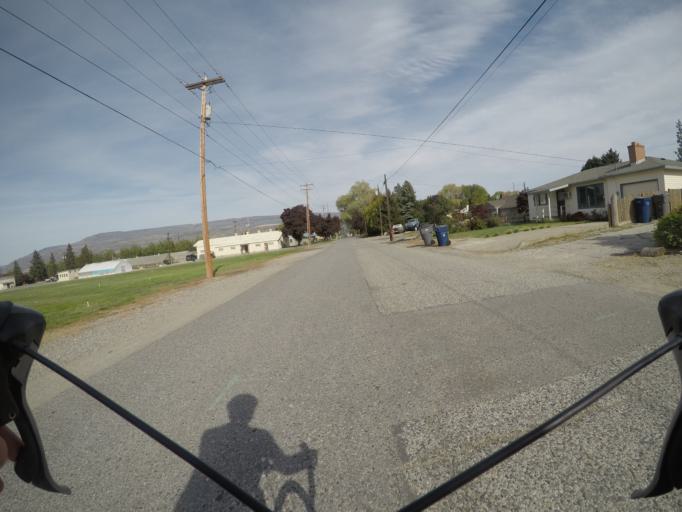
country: US
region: Washington
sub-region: Chelan County
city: West Wenatchee
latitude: 47.4371
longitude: -120.3486
